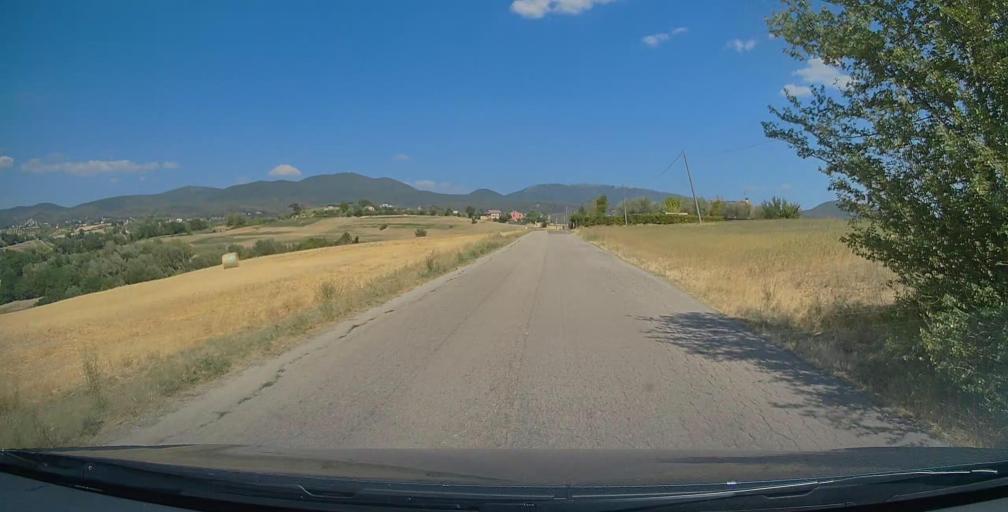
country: IT
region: Umbria
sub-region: Provincia di Terni
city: Otricoli
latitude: 42.4070
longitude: 12.5179
